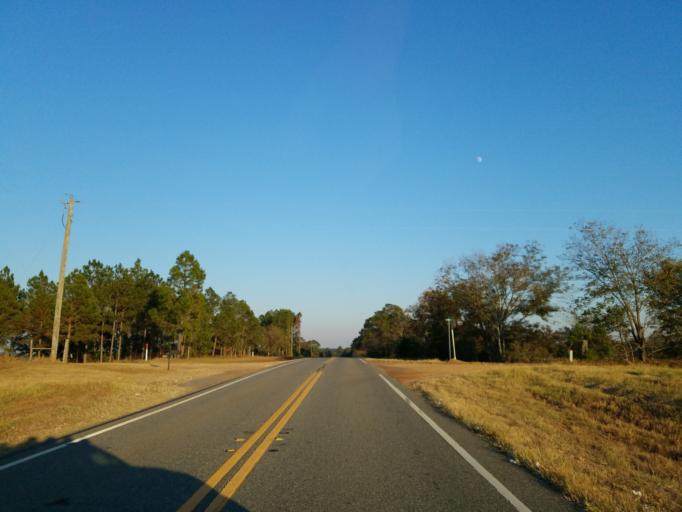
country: US
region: Georgia
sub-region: Wilcox County
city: Rochelle
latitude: 31.8534
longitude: -83.5738
